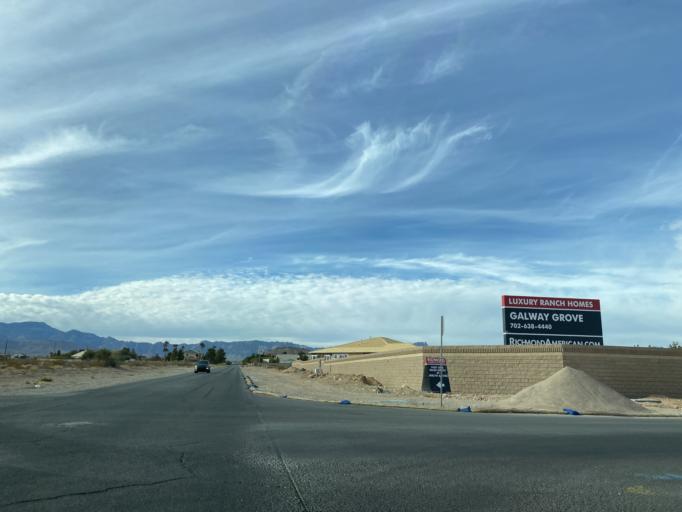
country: US
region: Nevada
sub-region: Clark County
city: Enterprise
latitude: 36.0336
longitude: -115.2697
